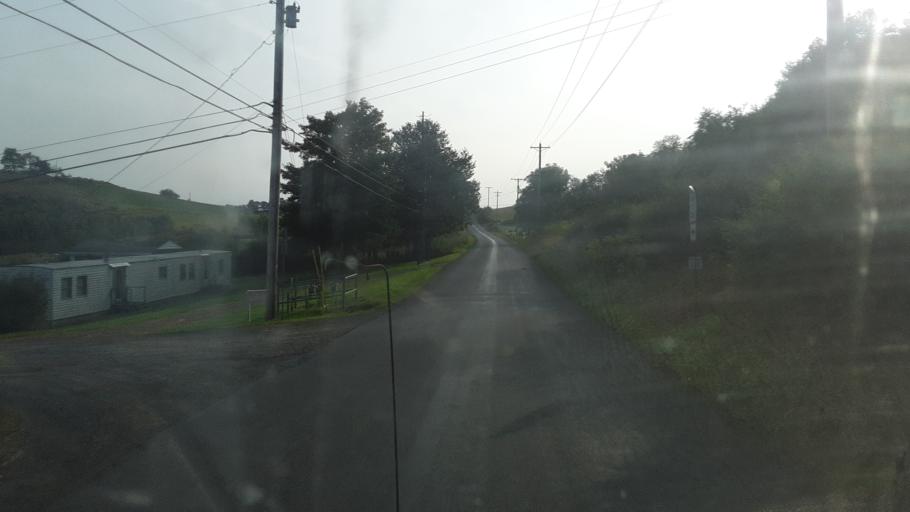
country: US
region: Pennsylvania
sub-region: Jefferson County
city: Punxsutawney
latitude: 40.9565
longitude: -79.1220
